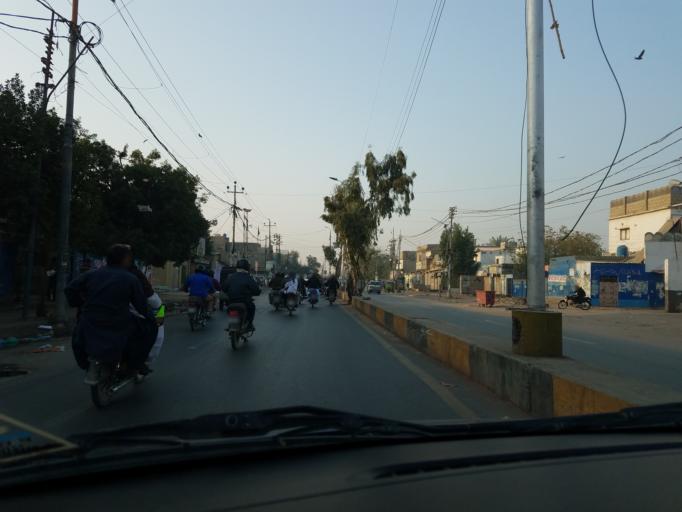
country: PK
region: Sindh
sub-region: Karachi District
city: Karachi
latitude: 24.8894
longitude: 67.0425
